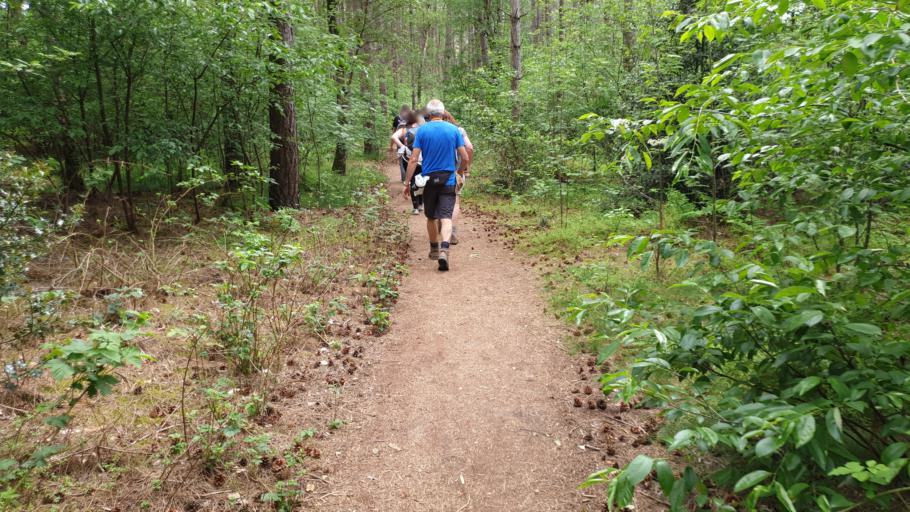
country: BE
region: Flanders
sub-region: Provincie Antwerpen
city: Meerhout
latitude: 51.1598
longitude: 5.0665
